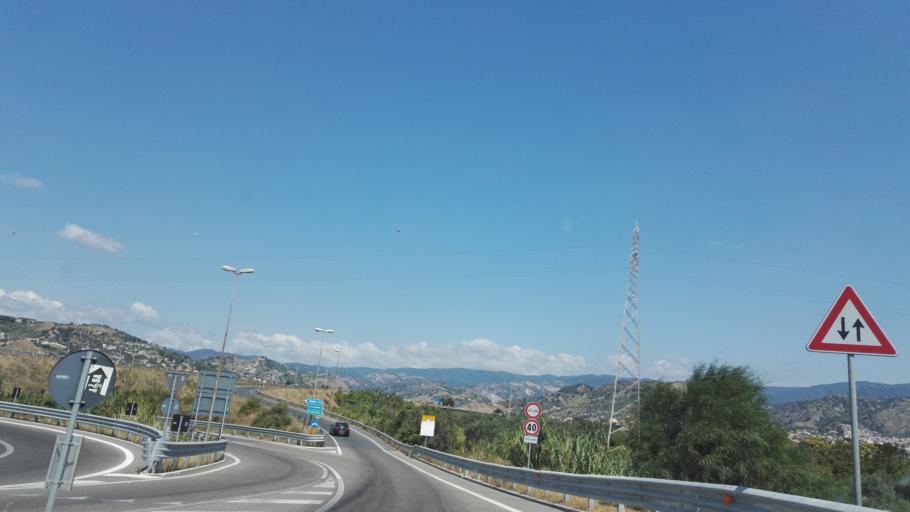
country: IT
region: Calabria
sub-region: Provincia di Reggio Calabria
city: Gioiosa Ionica
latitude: 38.3107
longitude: 16.3052
